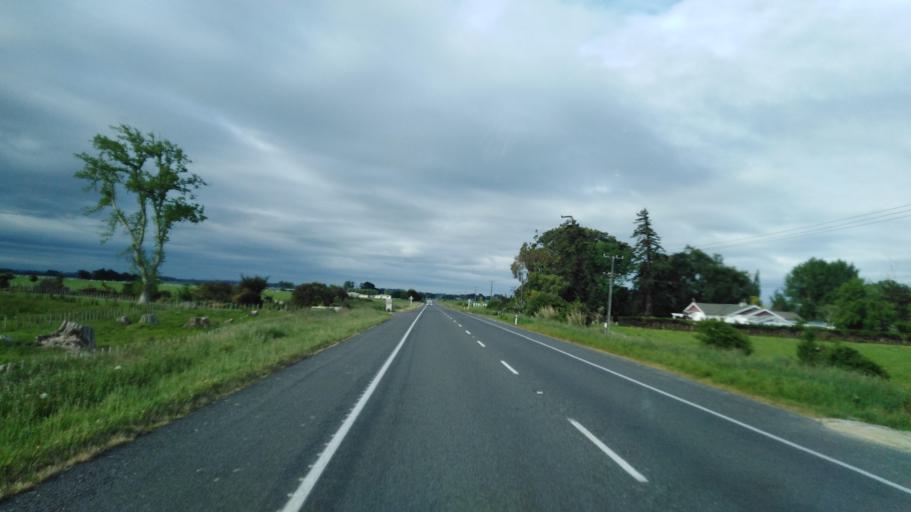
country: NZ
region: Manawatu-Wanganui
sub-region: Rangitikei District
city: Bulls
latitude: -40.2421
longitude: 175.4034
